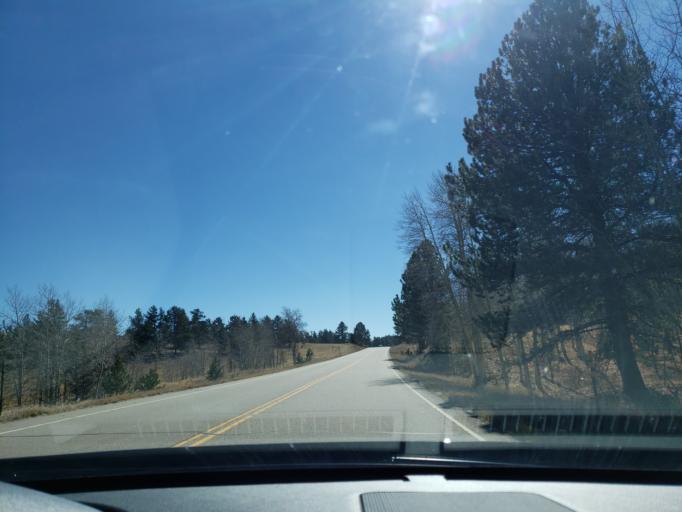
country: US
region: Colorado
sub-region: Chaffee County
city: Buena Vista
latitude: 38.8853
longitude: -105.6814
